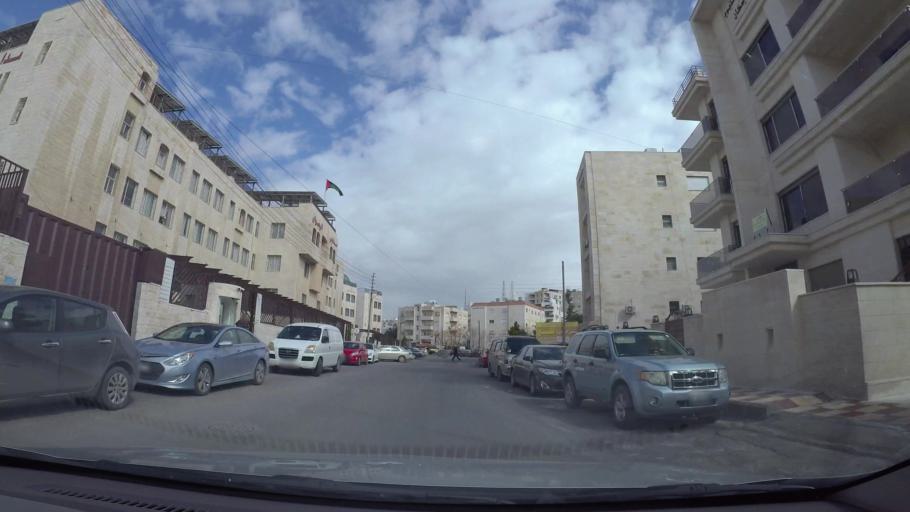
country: JO
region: Amman
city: Al Jubayhah
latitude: 31.9992
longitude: 35.8408
